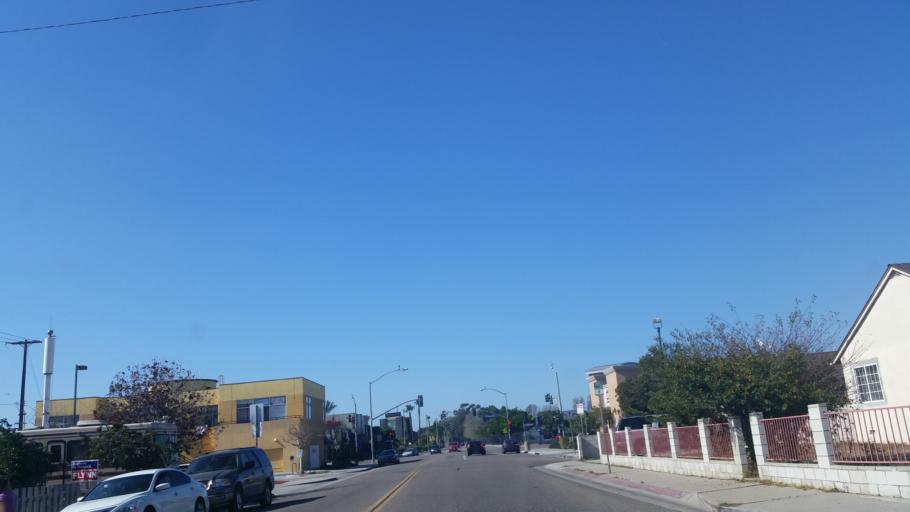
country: US
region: California
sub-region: Ventura County
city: Oxnard
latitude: 34.1773
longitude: -119.1763
